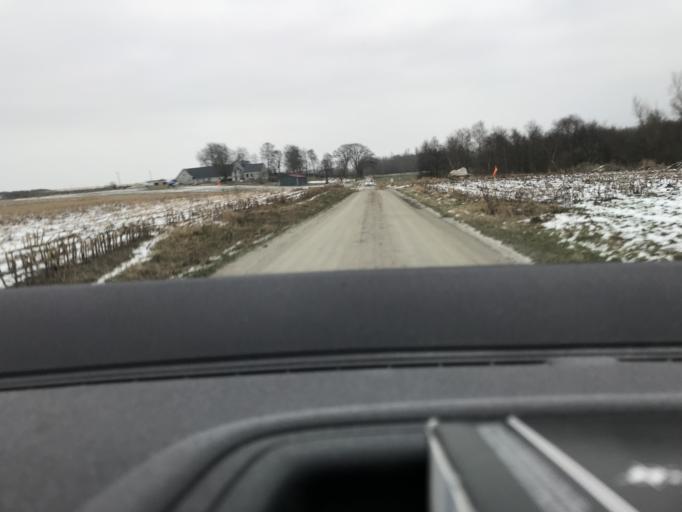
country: SE
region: Skane
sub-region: Ystads Kommun
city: Kopingebro
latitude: 55.4569
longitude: 13.8796
